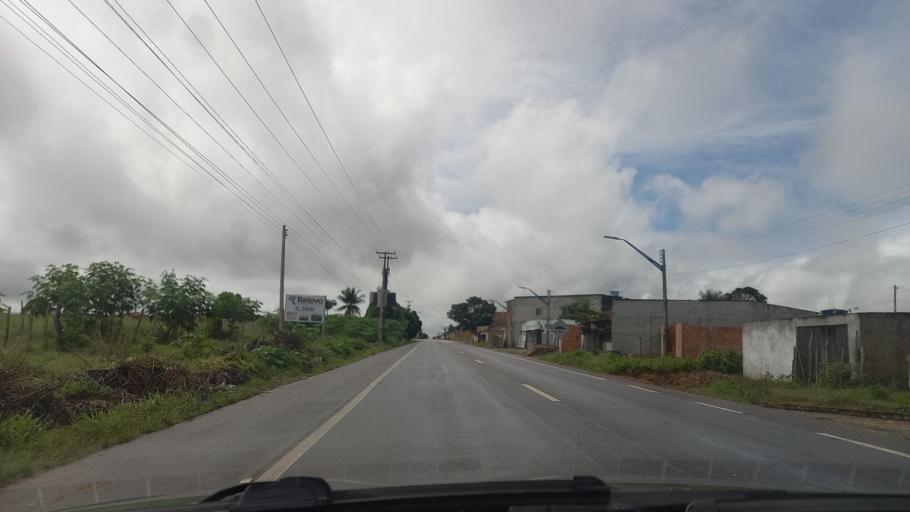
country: BR
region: Alagoas
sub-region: Limoeiro De Anadia
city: Limoeiro de Anadia
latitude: -9.7587
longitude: -36.5619
